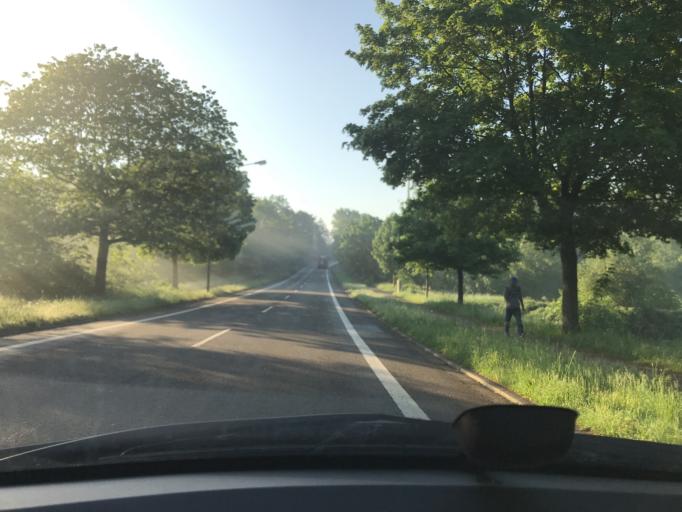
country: DE
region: Saarland
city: Saarlouis
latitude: 49.3392
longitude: 6.7661
